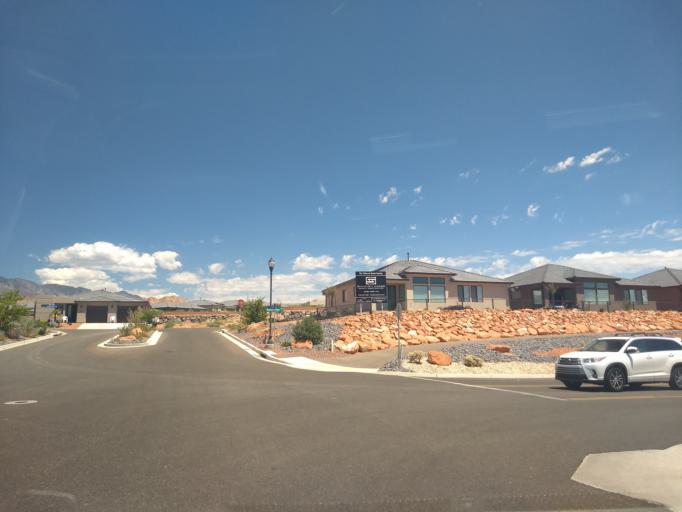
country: US
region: Utah
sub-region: Washington County
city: Washington
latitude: 37.1597
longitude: -113.5286
